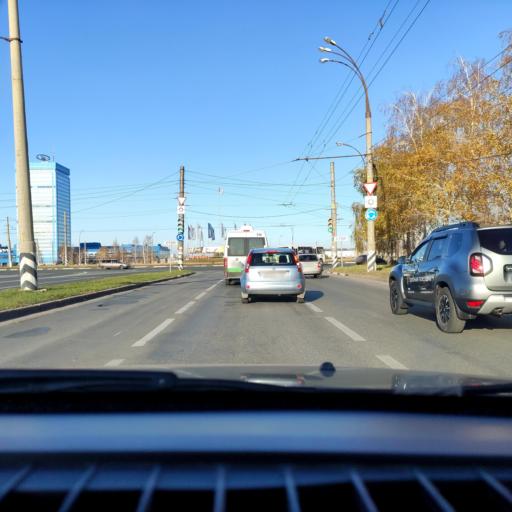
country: RU
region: Samara
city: Tol'yatti
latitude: 53.5510
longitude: 49.2668
